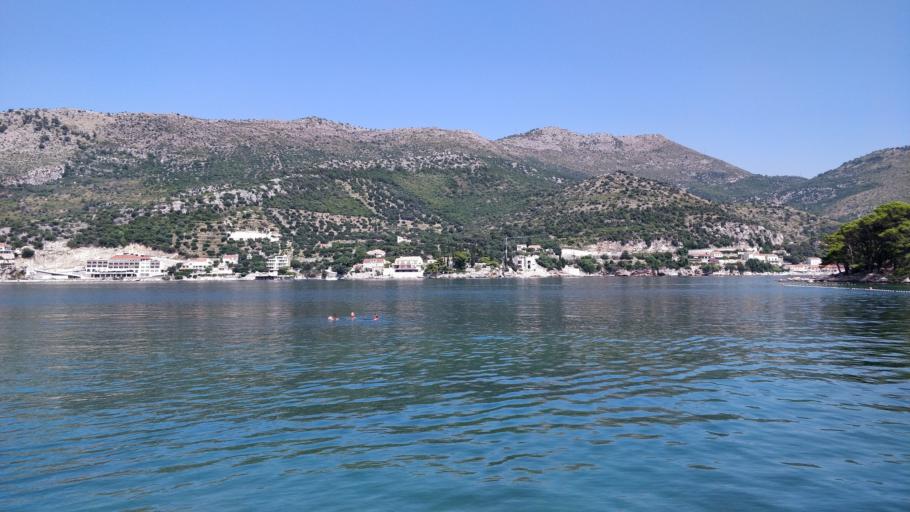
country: HR
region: Dubrovacko-Neretvanska
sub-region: Grad Dubrovnik
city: Mokosica
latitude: 42.6893
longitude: 18.0407
